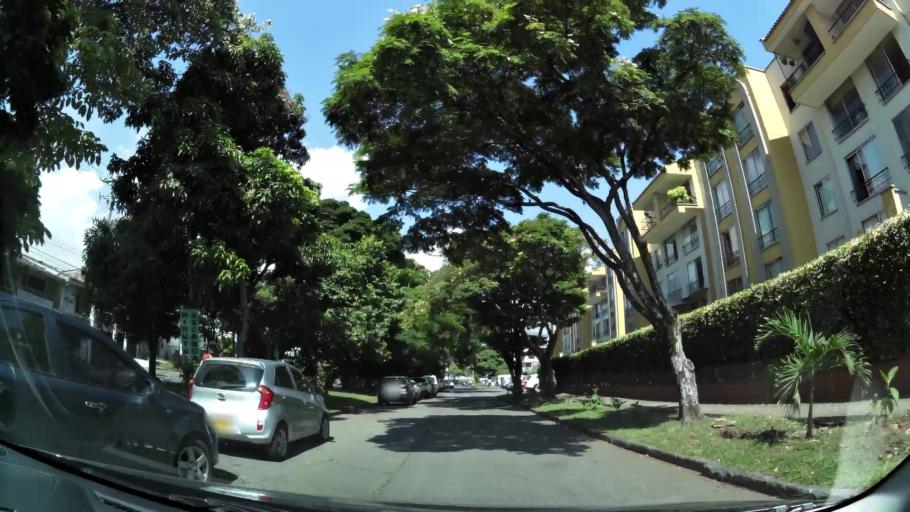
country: CO
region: Valle del Cauca
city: Cali
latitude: 3.4242
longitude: -76.5323
